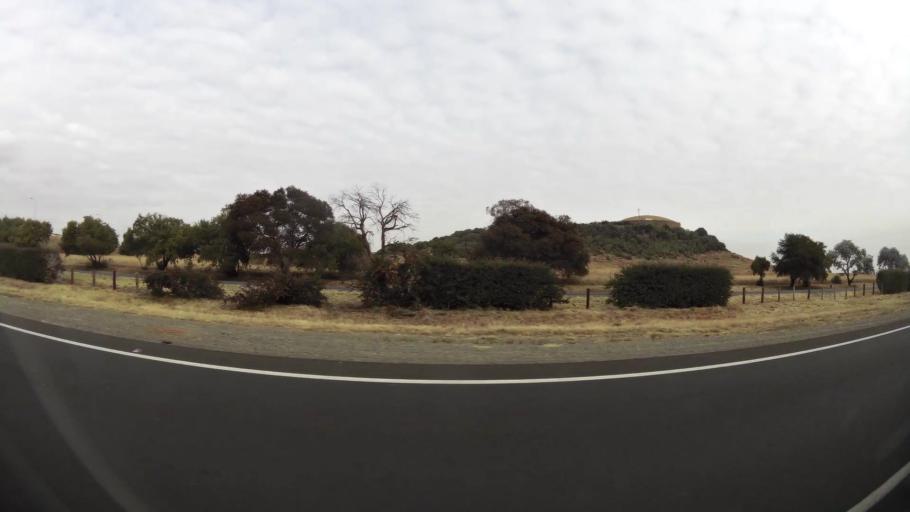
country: ZA
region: Orange Free State
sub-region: Mangaung Metropolitan Municipality
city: Bloemfontein
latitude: -29.1442
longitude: 26.1708
